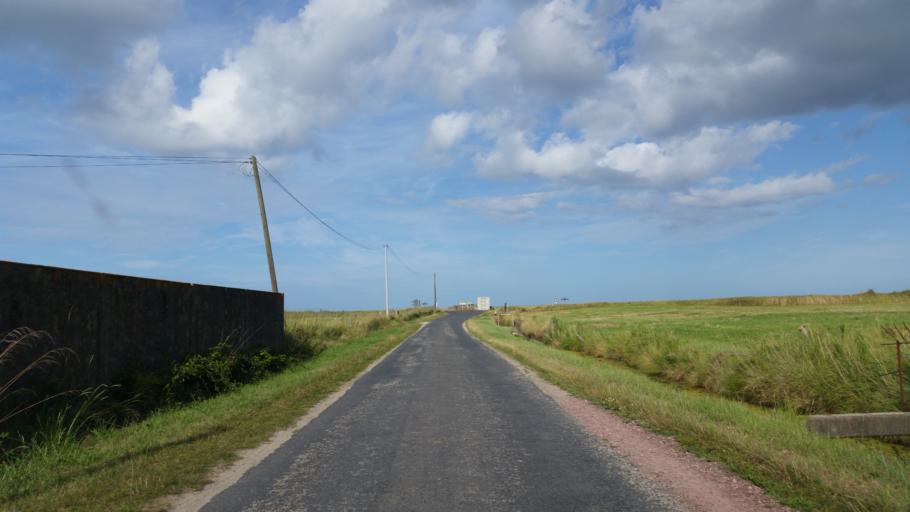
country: FR
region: Lower Normandy
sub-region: Departement de la Manche
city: Sainte-Mere-Eglise
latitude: 49.4586
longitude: -1.2284
